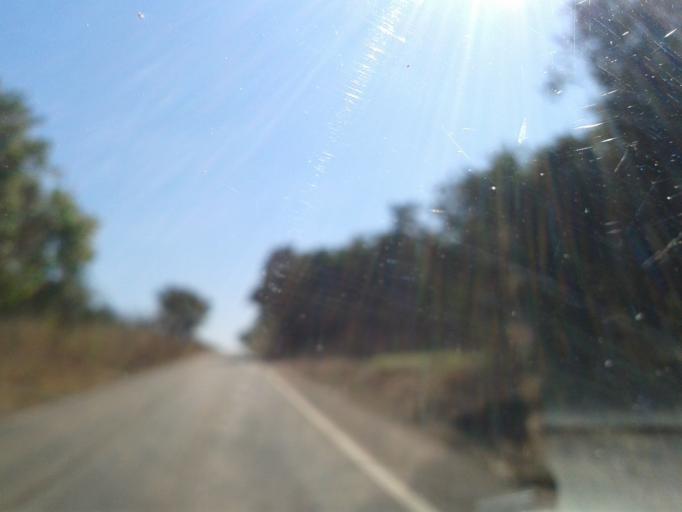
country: BR
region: Goias
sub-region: Mozarlandia
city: Mozarlandia
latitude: -14.4154
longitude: -50.4485
